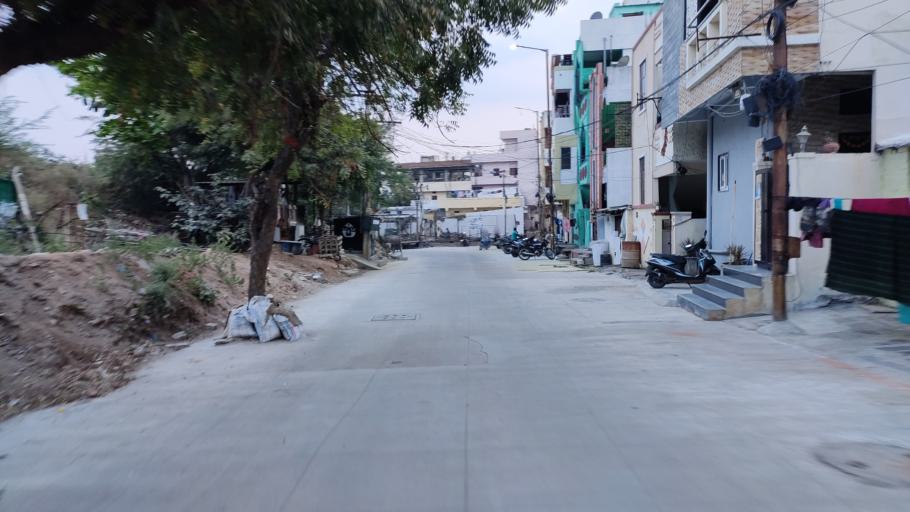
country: IN
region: Telangana
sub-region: Hyderabad
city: Malkajgiri
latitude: 17.4456
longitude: 78.5234
